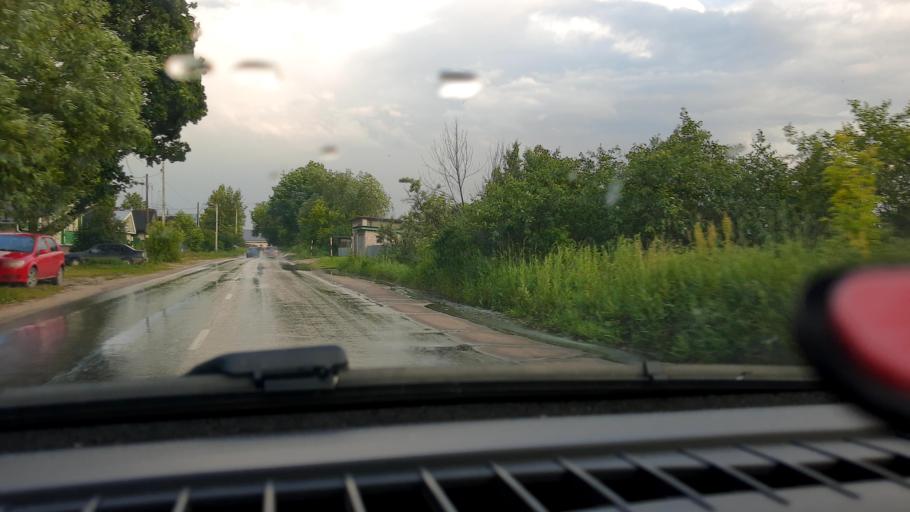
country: RU
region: Nizjnij Novgorod
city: Gorodets
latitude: 56.6663
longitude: 43.4549
